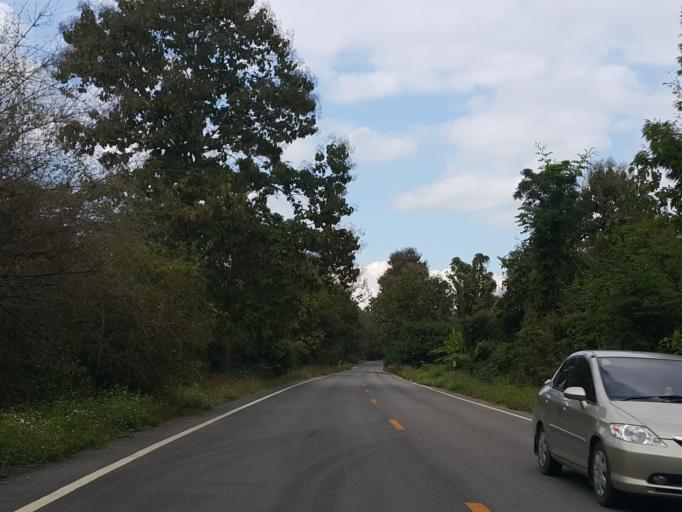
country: TH
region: Lampang
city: Chae Hom
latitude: 18.6135
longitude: 99.4822
